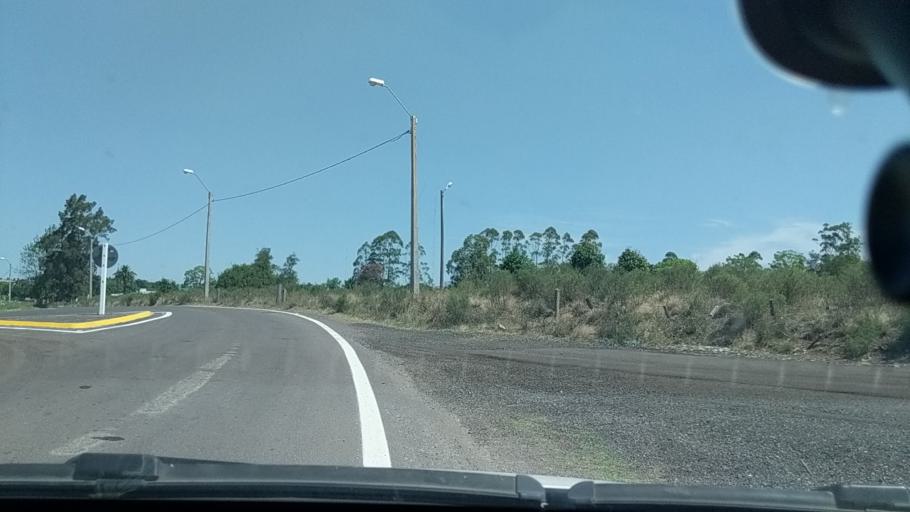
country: UY
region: Tacuarembo
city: Paso de los Toros
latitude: -32.8027
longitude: -56.5128
